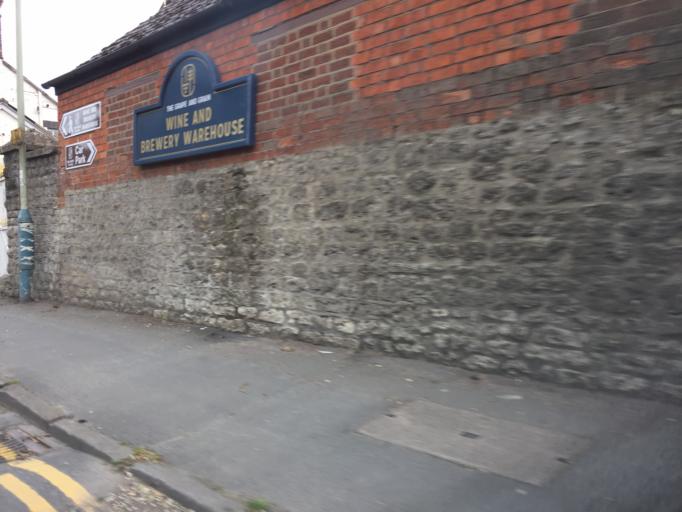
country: GB
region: England
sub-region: Borough of Swindon
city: Broad Blunsdon
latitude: 51.5925
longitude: -1.7624
